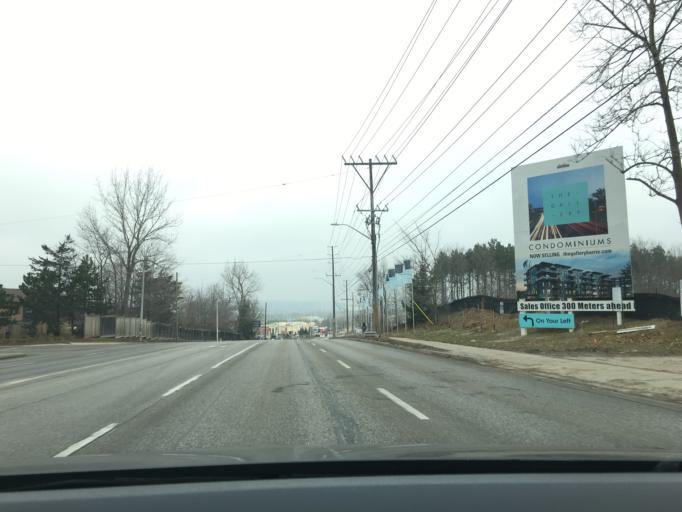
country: CA
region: Ontario
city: Barrie
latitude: 44.3544
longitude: -79.6994
